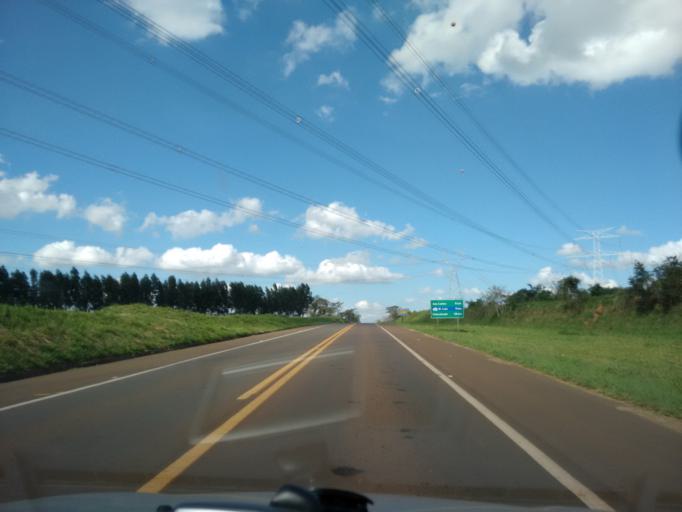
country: BR
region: Sao Paulo
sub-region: Sao Carlos
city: Sao Carlos
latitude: -22.0641
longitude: -47.9341
